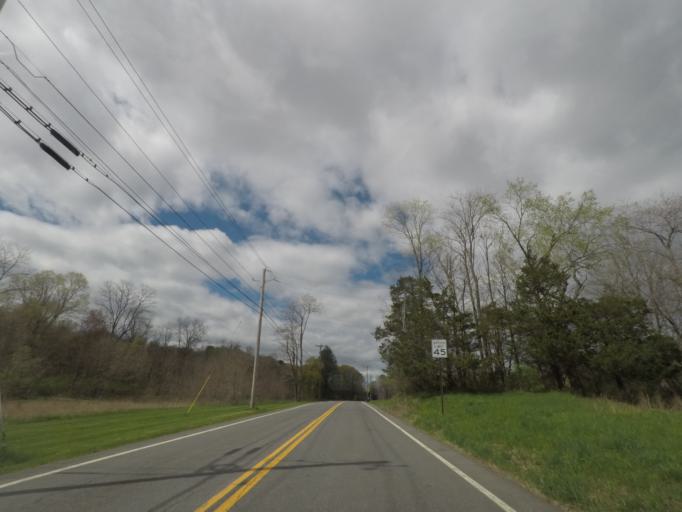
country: US
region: New York
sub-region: Columbia County
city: Philmont
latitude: 42.2611
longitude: -73.6659
